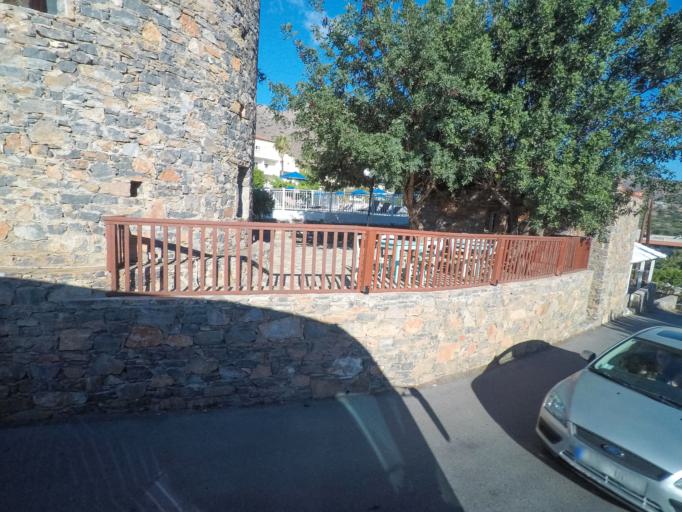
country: GR
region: Crete
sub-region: Nomos Lasithiou
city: Skhisma
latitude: 35.2466
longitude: 25.7299
